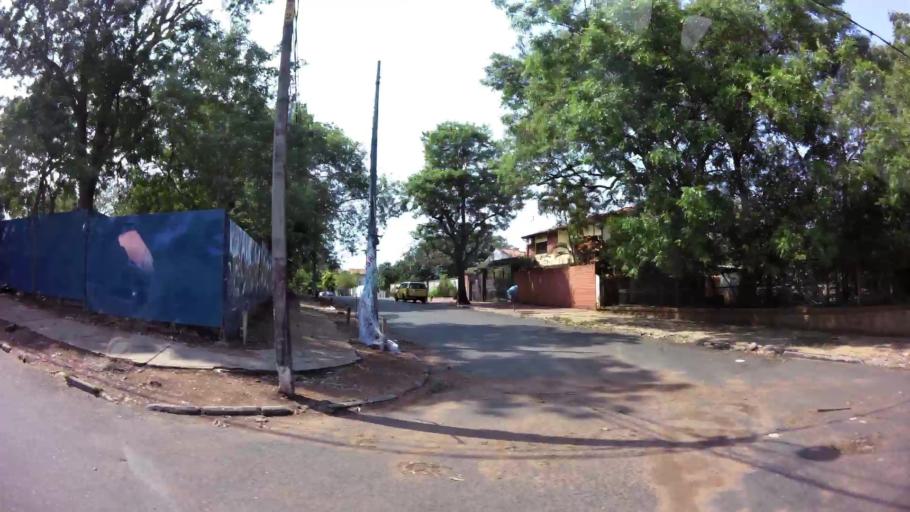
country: PY
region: Asuncion
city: Asuncion
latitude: -25.2929
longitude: -57.6552
